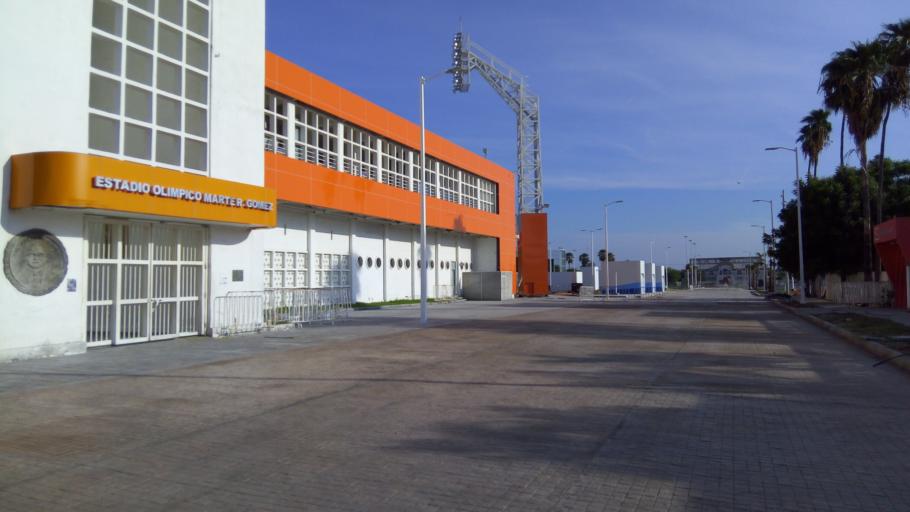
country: MX
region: Tamaulipas
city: Ciudad Victoria
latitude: 23.7392
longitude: -99.1517
